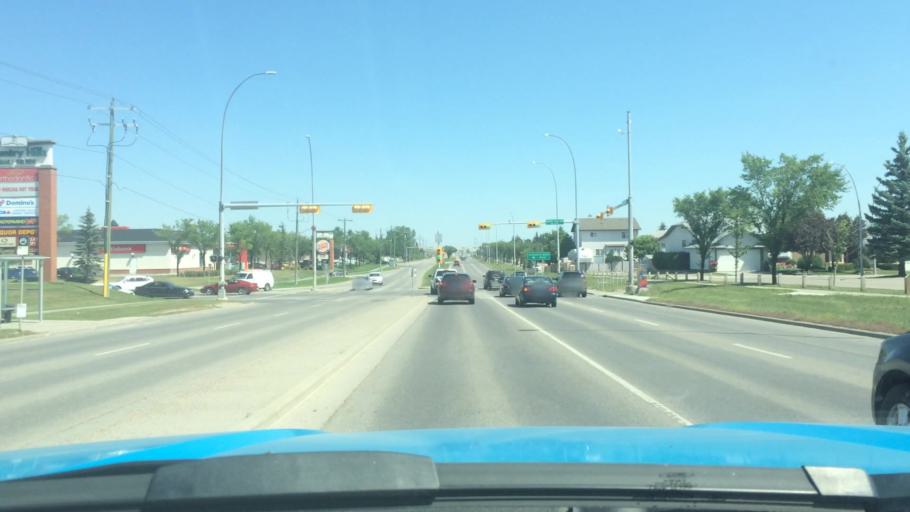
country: CA
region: Alberta
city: Calgary
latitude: 51.1542
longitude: -114.0571
